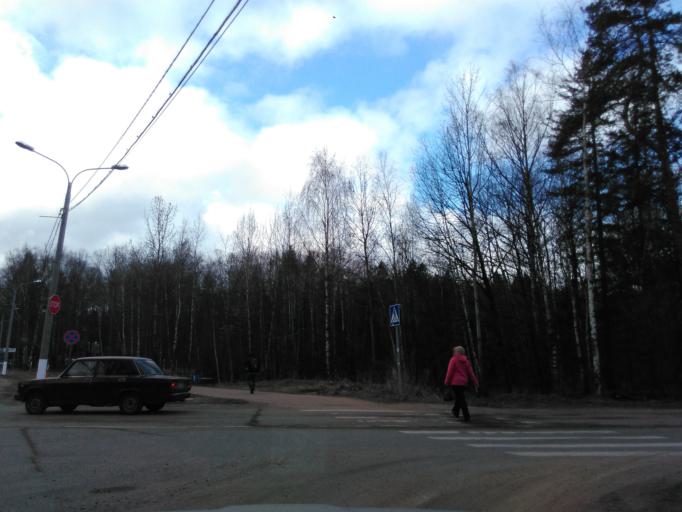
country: RU
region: Moskovskaya
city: Mendeleyevo
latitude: 56.0116
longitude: 37.2213
